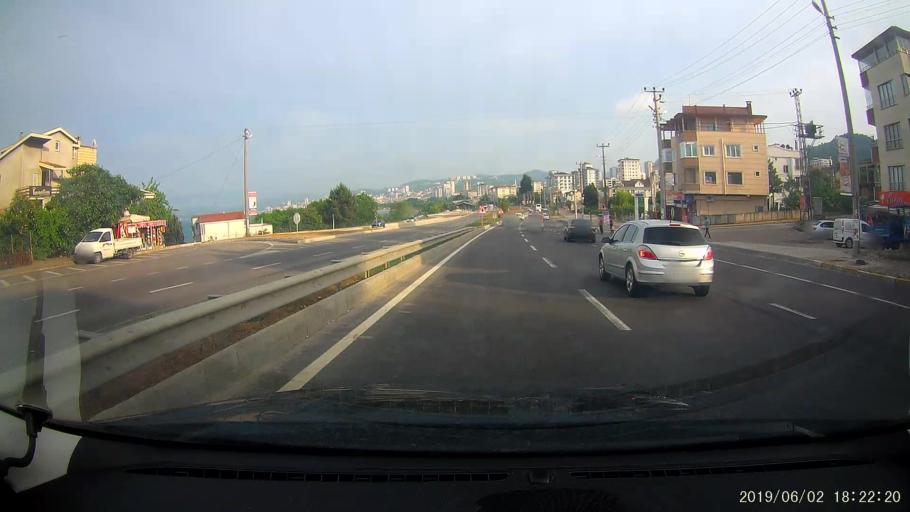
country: TR
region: Ordu
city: Fatsa
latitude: 41.0583
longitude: 37.4769
